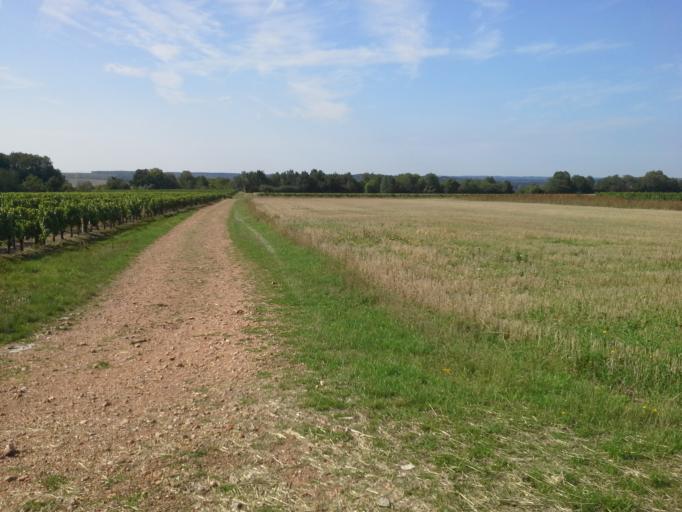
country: FR
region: Centre
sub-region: Departement du Loir-et-Cher
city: Villiers-sur-Loir
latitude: 47.8153
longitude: 0.9803
